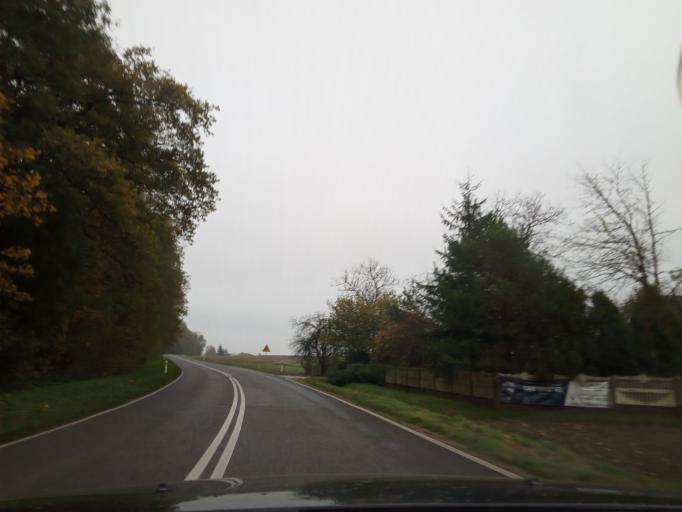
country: PL
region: Lesser Poland Voivodeship
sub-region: Powiat proszowicki
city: Klimontow
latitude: 50.2320
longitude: 20.3867
